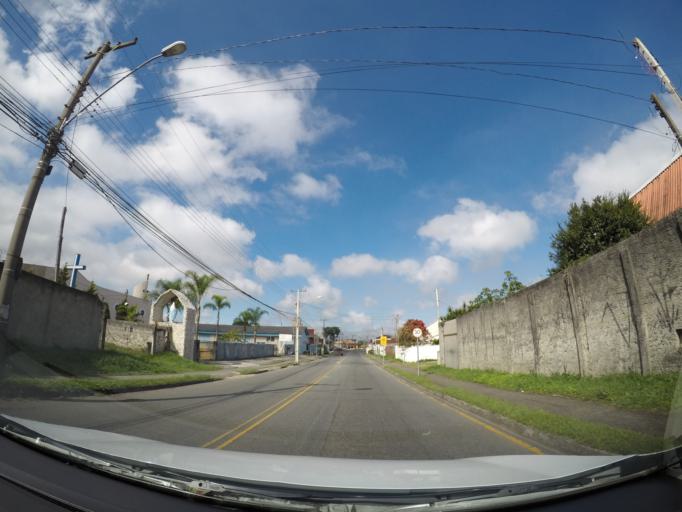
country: BR
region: Parana
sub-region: Sao Jose Dos Pinhais
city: Sao Jose dos Pinhais
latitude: -25.4948
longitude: -49.2160
